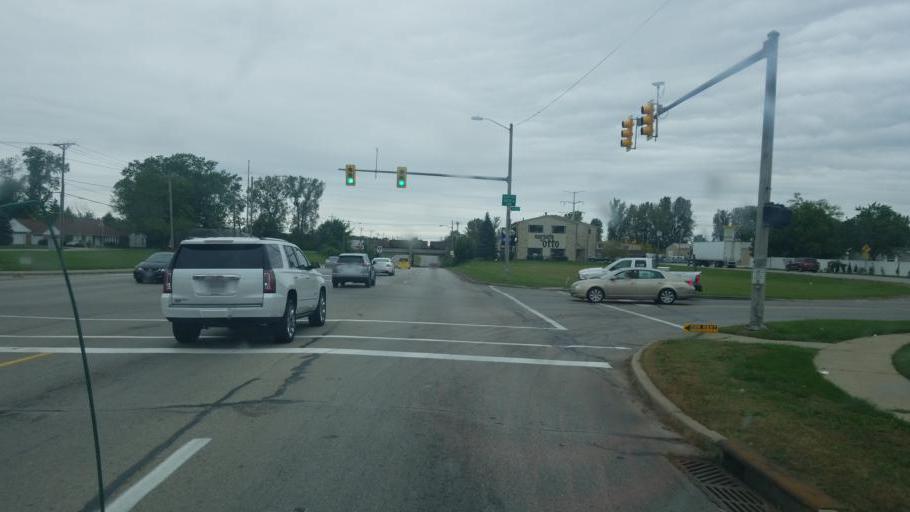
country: US
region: Ohio
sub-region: Lucas County
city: Ottawa Hills
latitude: 41.6222
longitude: -83.6644
